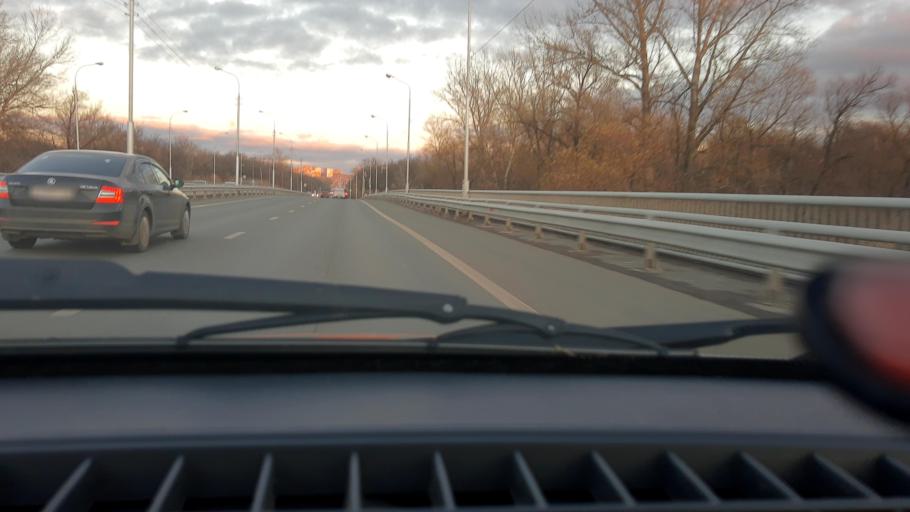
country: RU
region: Bashkortostan
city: Ufa
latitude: 54.7001
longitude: 55.9147
